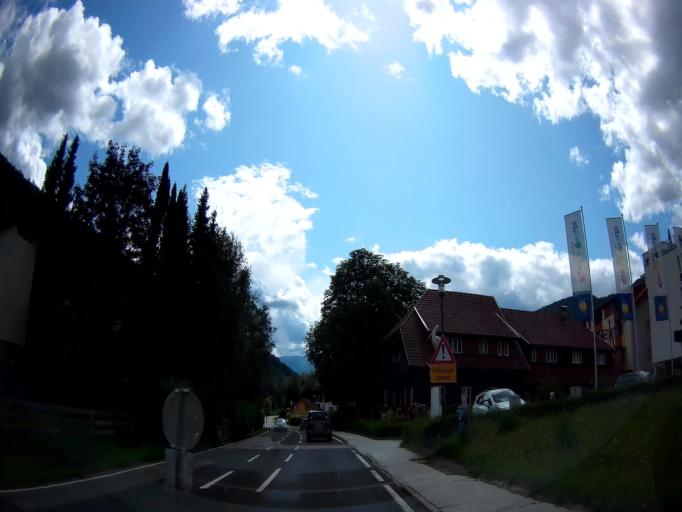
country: AT
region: Carinthia
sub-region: Politischer Bezirk Spittal an der Drau
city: Trebesing
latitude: 46.8830
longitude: 13.5140
